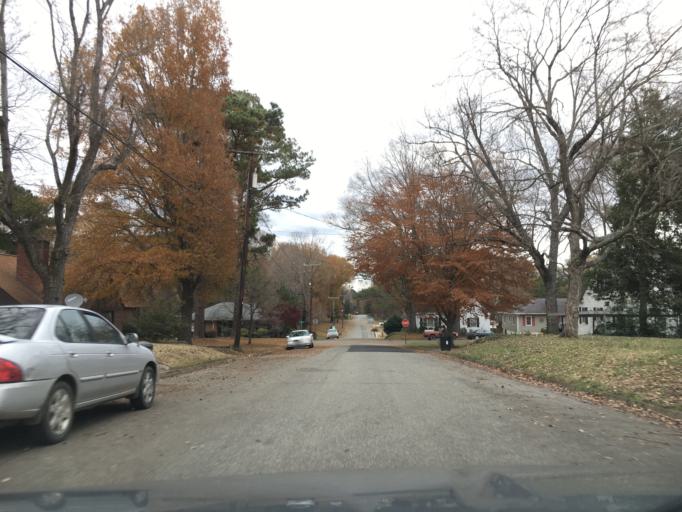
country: US
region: Virginia
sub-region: Halifax County
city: South Boston
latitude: 36.7060
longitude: -78.8962
